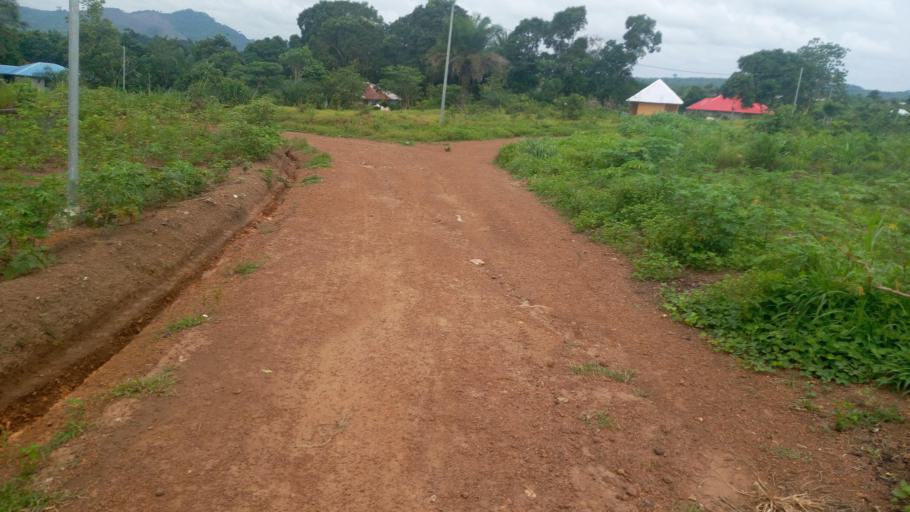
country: SL
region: Southern Province
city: Mogbwemo
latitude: 7.7829
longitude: -12.3009
